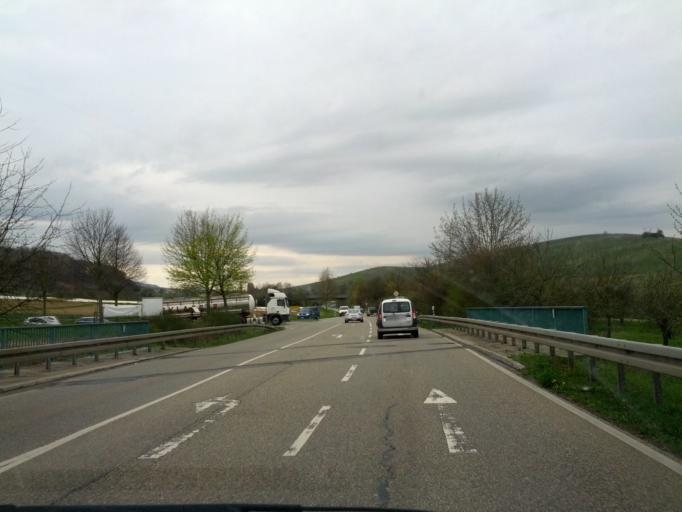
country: DE
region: Baden-Wuerttemberg
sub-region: Freiburg Region
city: Schallstadt
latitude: 47.9567
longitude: 7.7657
